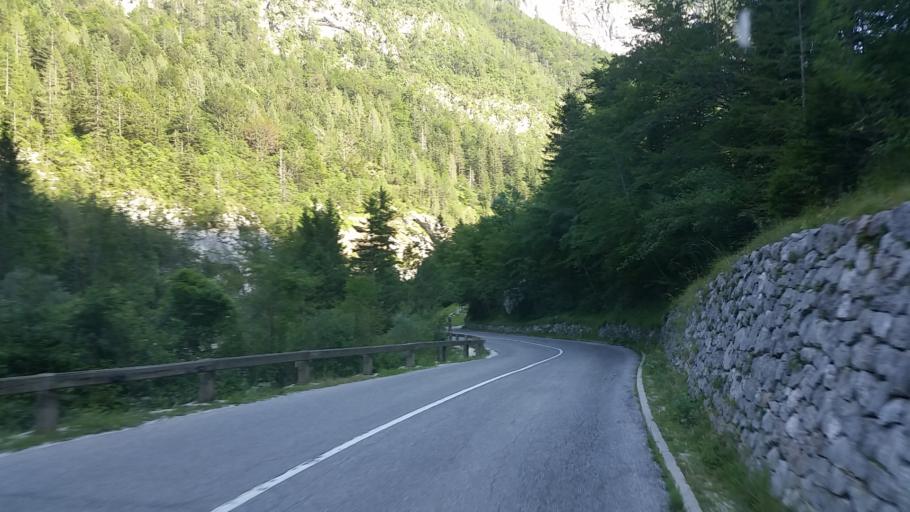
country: SI
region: Kranjska Gora
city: Kranjska Gora
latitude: 46.4023
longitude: 13.7423
